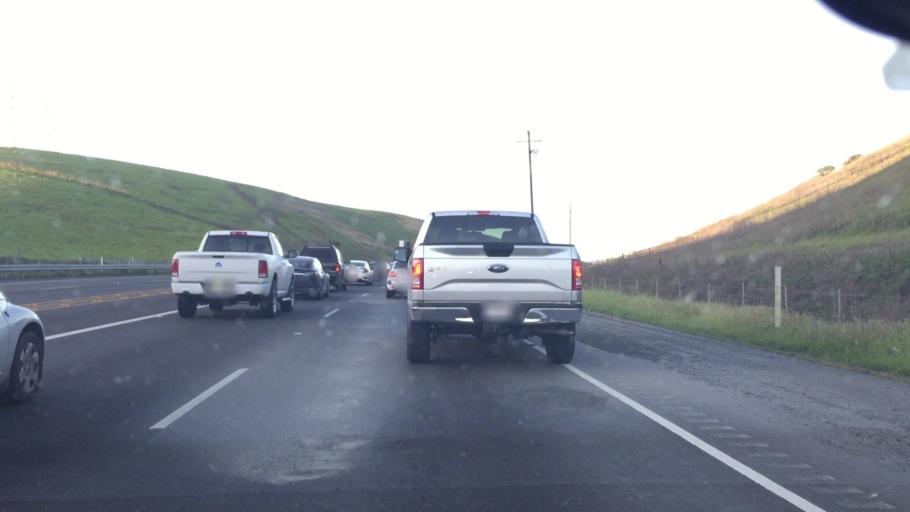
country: US
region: California
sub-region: Alameda County
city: Livermore
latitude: 37.6209
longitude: -121.8096
